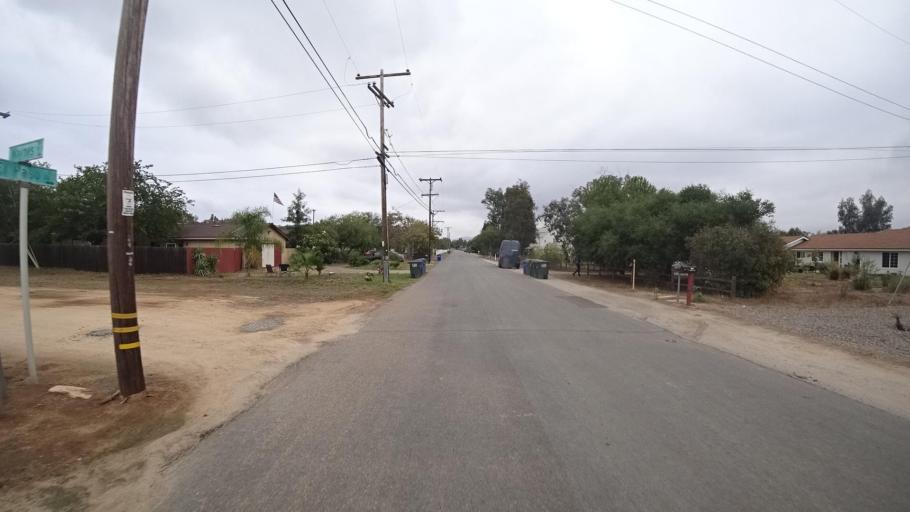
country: US
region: California
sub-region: San Diego County
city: Ramona
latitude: 33.0462
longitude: -116.9012
